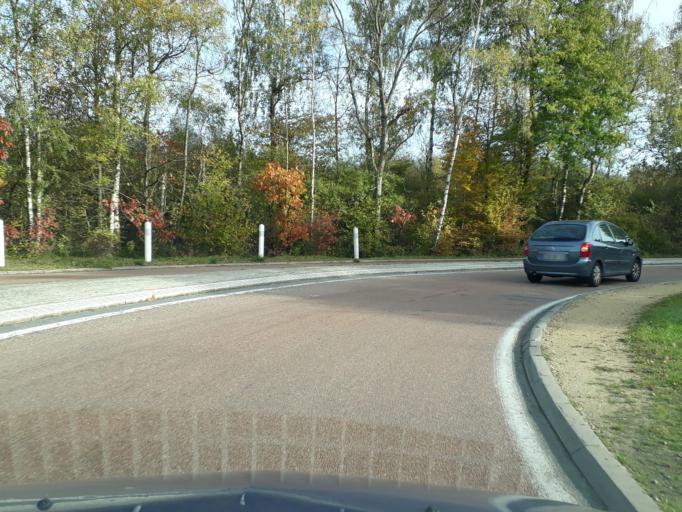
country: FR
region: Ile-de-France
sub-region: Departement de Seine-et-Marne
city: La Grande-Paroisse
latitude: 48.4184
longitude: 2.9156
